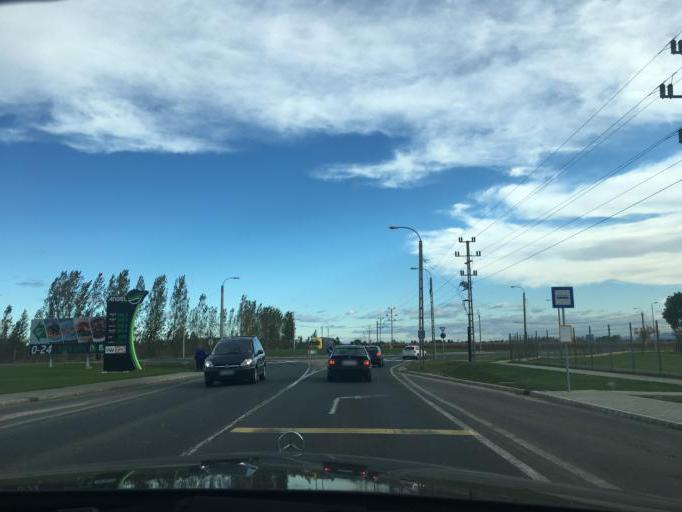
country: HU
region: Borsod-Abauj-Zemplen
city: Szikszo
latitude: 48.1758
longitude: 20.9150
